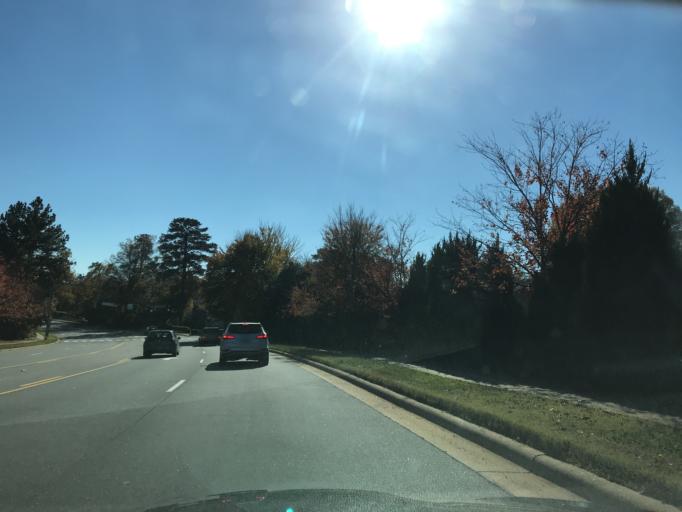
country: US
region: North Carolina
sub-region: Wake County
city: Raleigh
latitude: 35.8596
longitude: -78.6013
